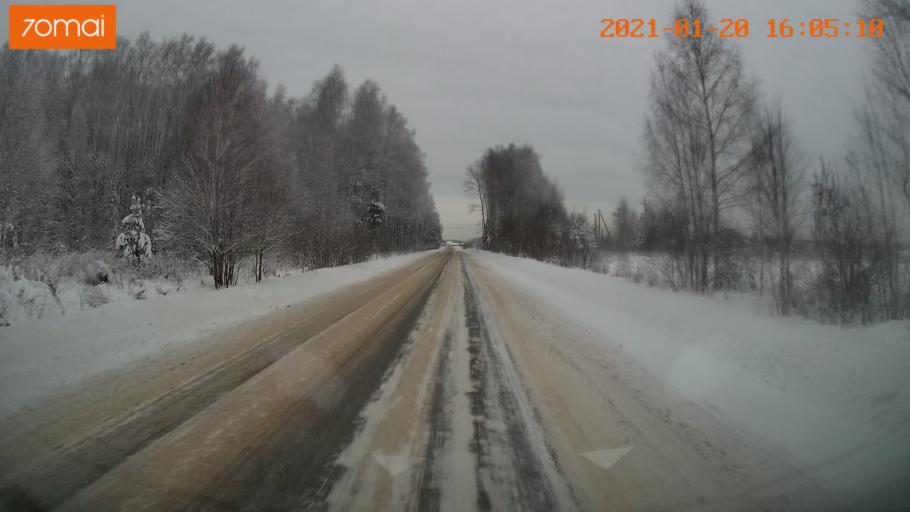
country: RU
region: Vladimir
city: Sudogda
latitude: 56.0632
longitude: 40.8091
